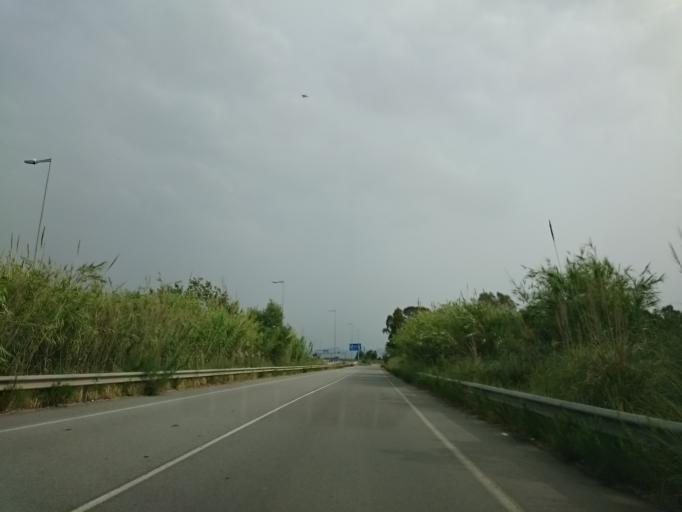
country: ES
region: Catalonia
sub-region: Provincia de Barcelona
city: Viladecans
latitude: 41.2805
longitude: 2.0526
